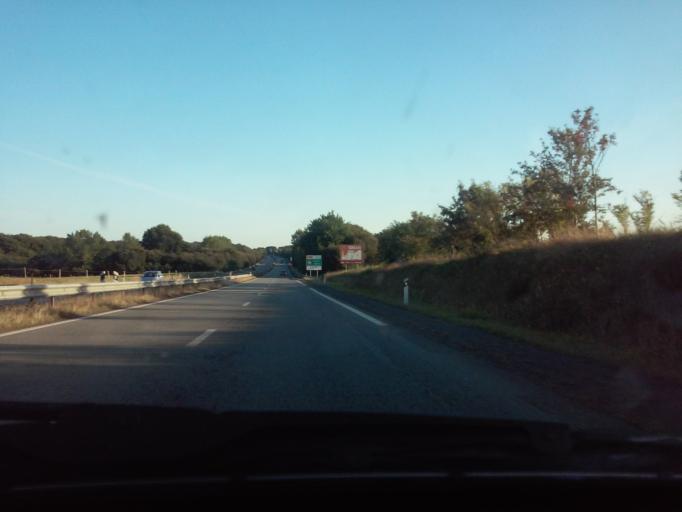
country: FR
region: Brittany
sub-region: Departement des Cotes-d'Armor
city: Saint-Samson-sur-Rance
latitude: 48.5009
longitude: -2.0399
